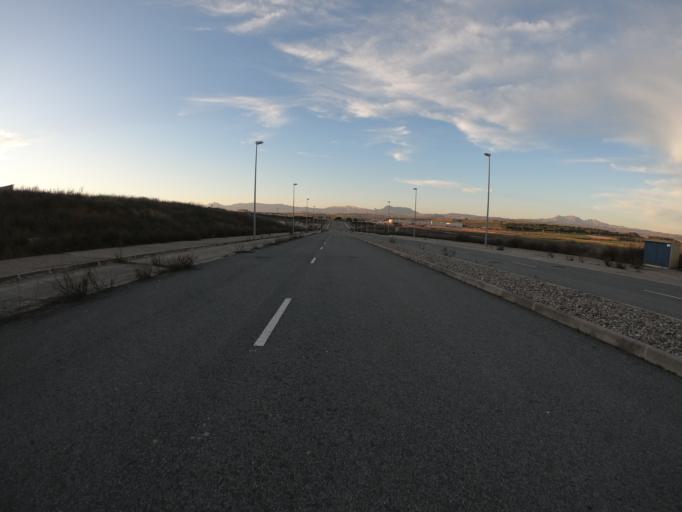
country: ES
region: Basque Country
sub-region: Provincia de Alava
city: Oyon
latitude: 42.4826
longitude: -2.4138
